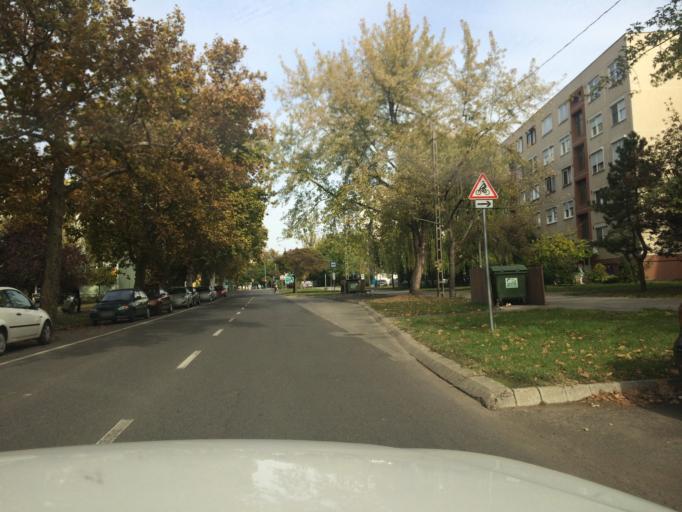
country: HU
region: Szabolcs-Szatmar-Bereg
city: Nyiregyhaza
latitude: 47.9634
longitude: 21.7114
